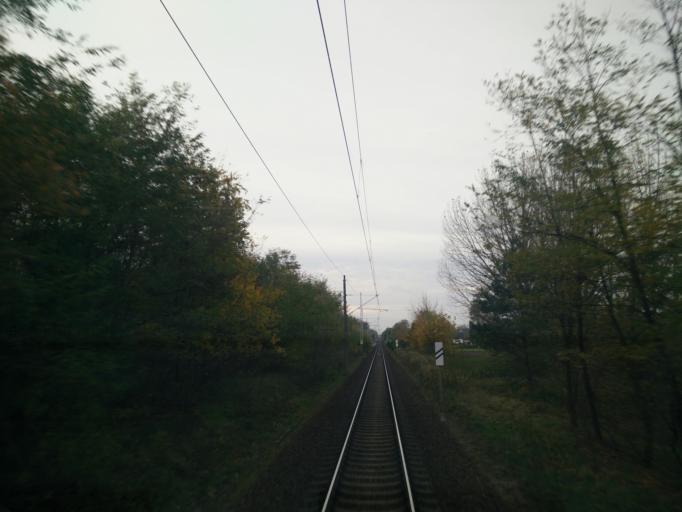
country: DE
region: Brandenburg
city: Vetschau
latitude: 51.8135
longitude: 14.0354
